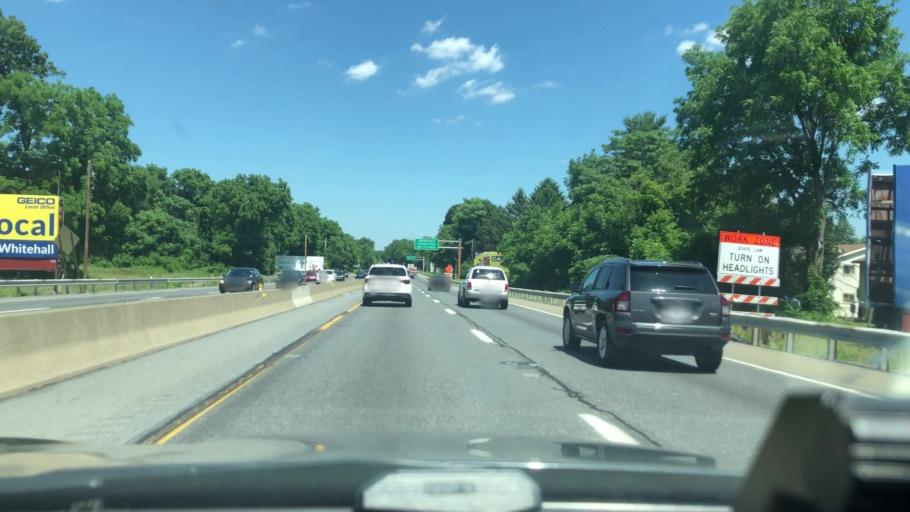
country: US
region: Pennsylvania
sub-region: Lehigh County
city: Allentown
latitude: 40.6123
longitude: -75.5160
